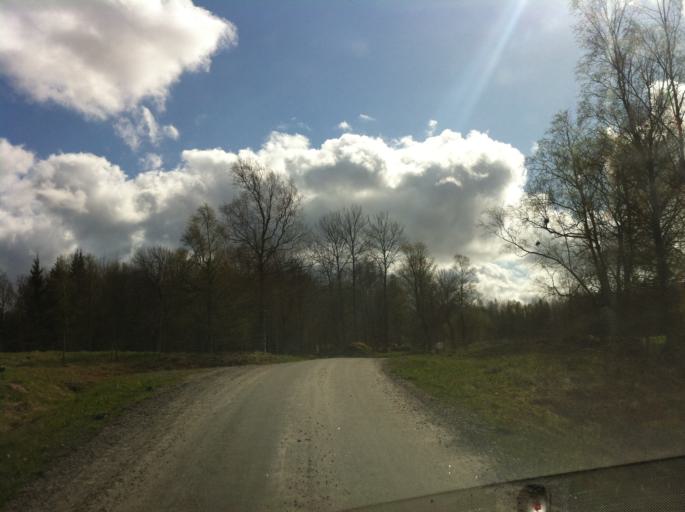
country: SE
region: Vaestra Goetaland
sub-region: Bollebygds Kommun
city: Bollebygd
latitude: 57.7702
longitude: 12.5920
